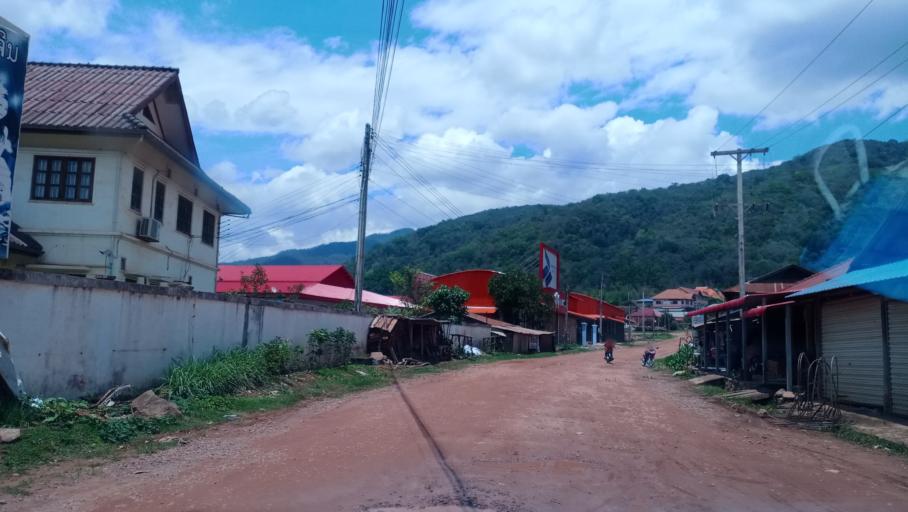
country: CN
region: Yunnan
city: Menglie
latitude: 22.1256
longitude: 101.7903
